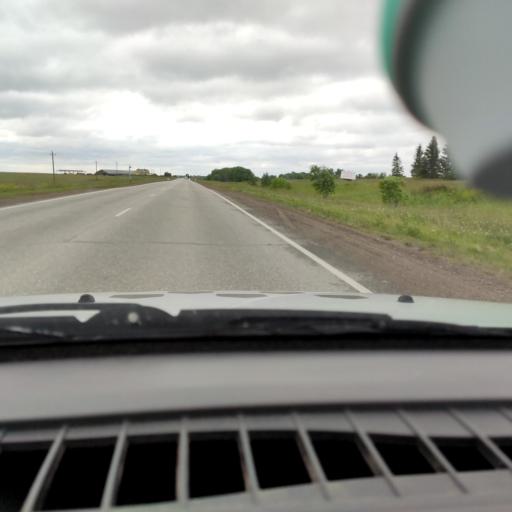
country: RU
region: Perm
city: Polazna
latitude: 58.3650
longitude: 56.4817
